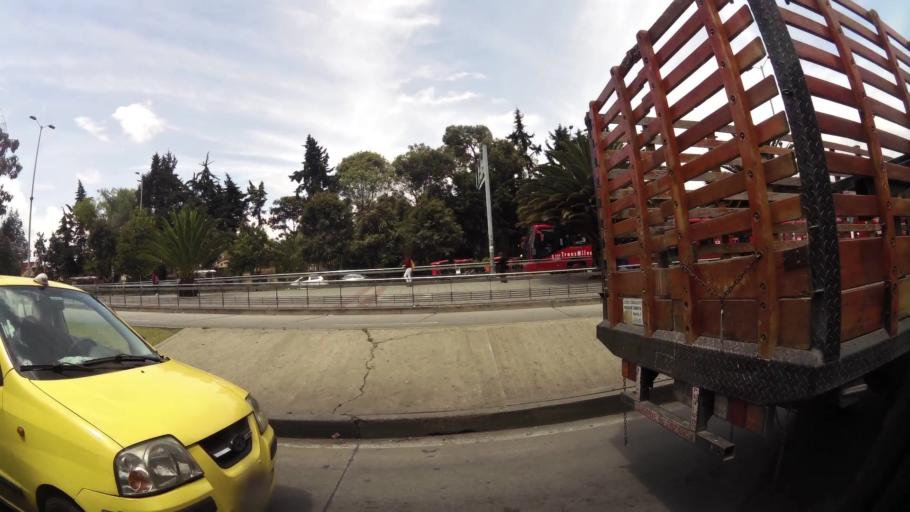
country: CO
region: Cundinamarca
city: Cota
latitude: 4.7419
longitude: -74.0906
